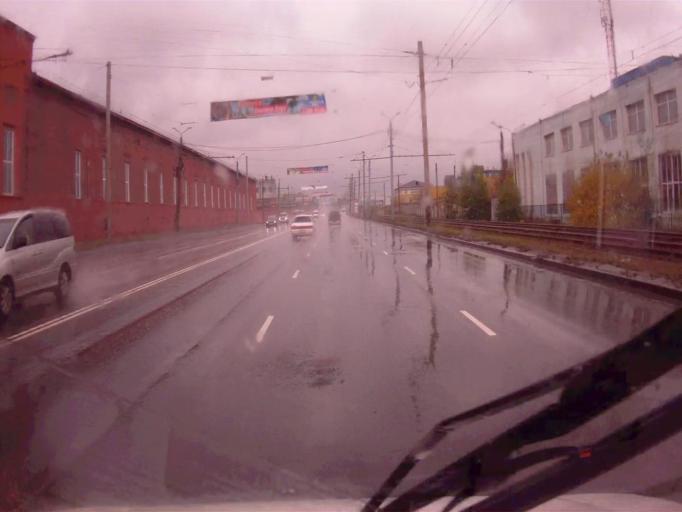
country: RU
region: Chelyabinsk
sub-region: Gorod Chelyabinsk
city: Chelyabinsk
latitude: 55.2080
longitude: 61.3841
